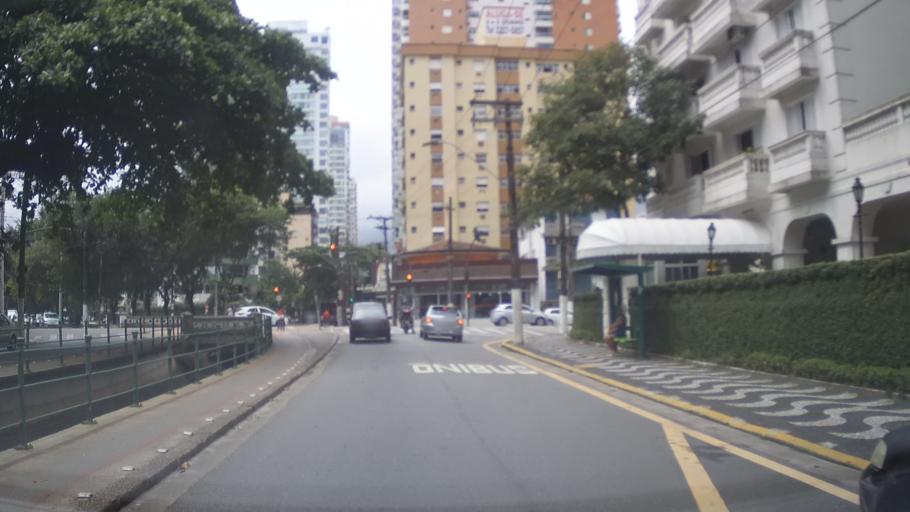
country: BR
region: Sao Paulo
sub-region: Santos
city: Santos
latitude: -23.9731
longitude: -46.3205
